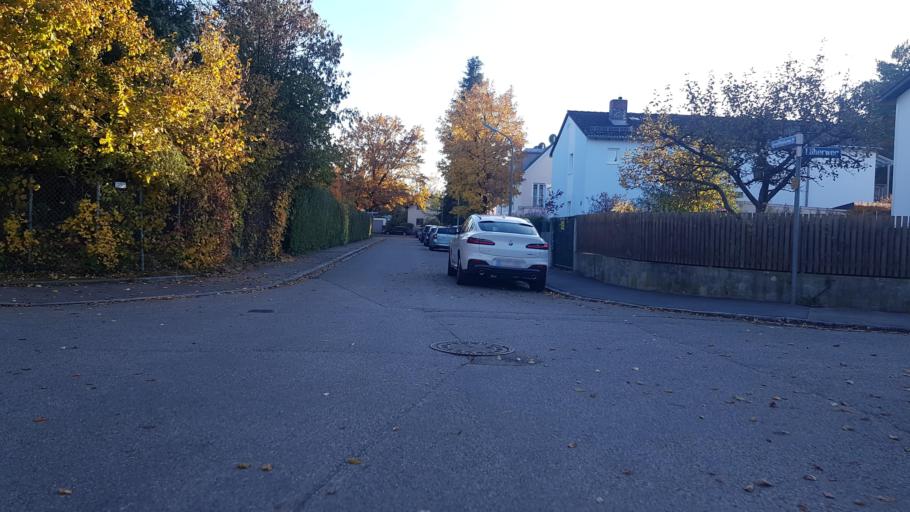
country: DE
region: Bavaria
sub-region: Upper Bavaria
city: Karlsfeld
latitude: 48.1828
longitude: 11.4834
